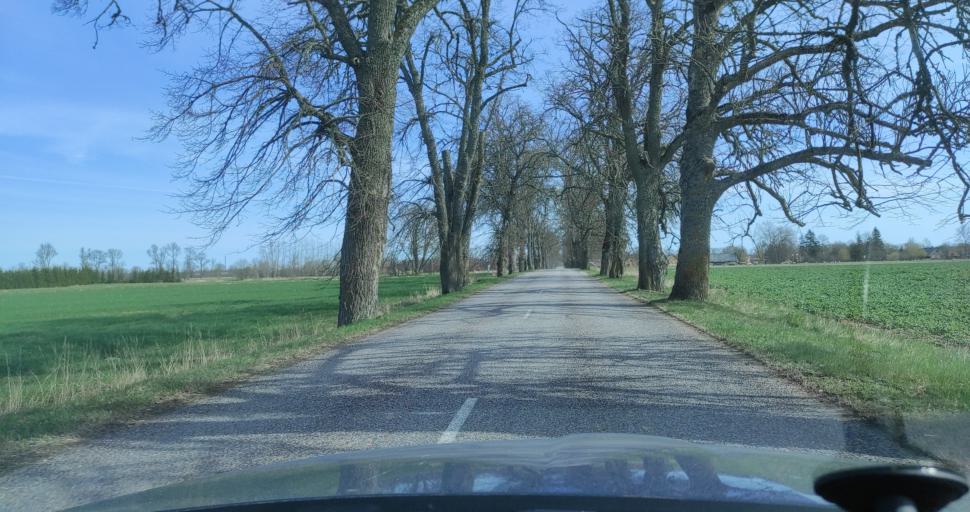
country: LV
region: Talsu Rajons
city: Stende
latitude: 57.2187
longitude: 22.5051
